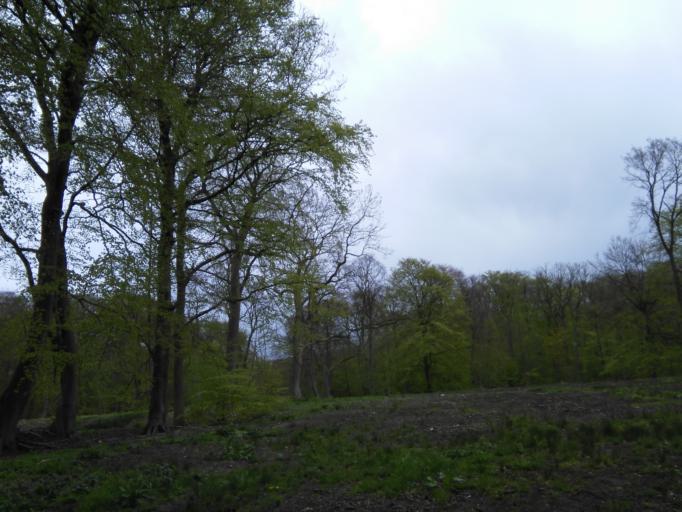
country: DK
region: Central Jutland
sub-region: Arhus Kommune
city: Arhus
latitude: 56.1353
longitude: 10.1920
